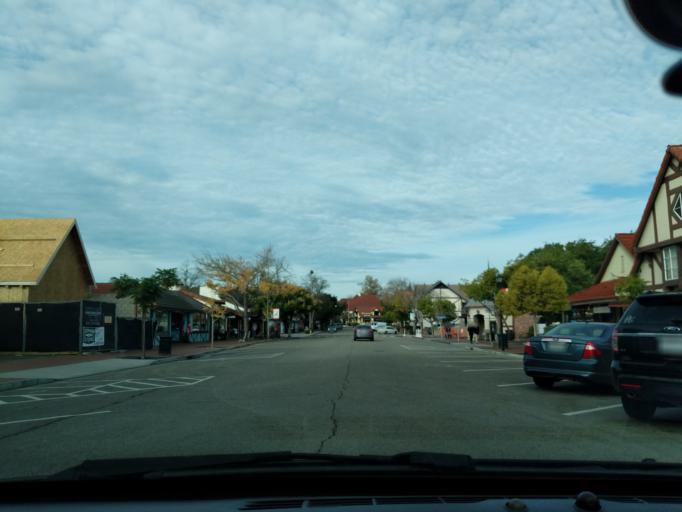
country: US
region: California
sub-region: Santa Barbara County
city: Solvang
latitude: 34.5950
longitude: -120.1400
